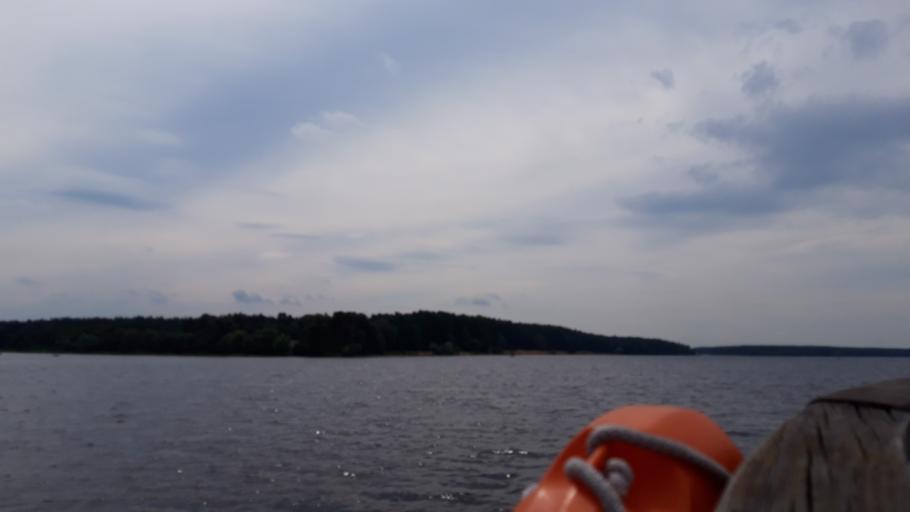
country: RU
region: Tverskaya
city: Konakovo
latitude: 56.7119
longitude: 36.7555
